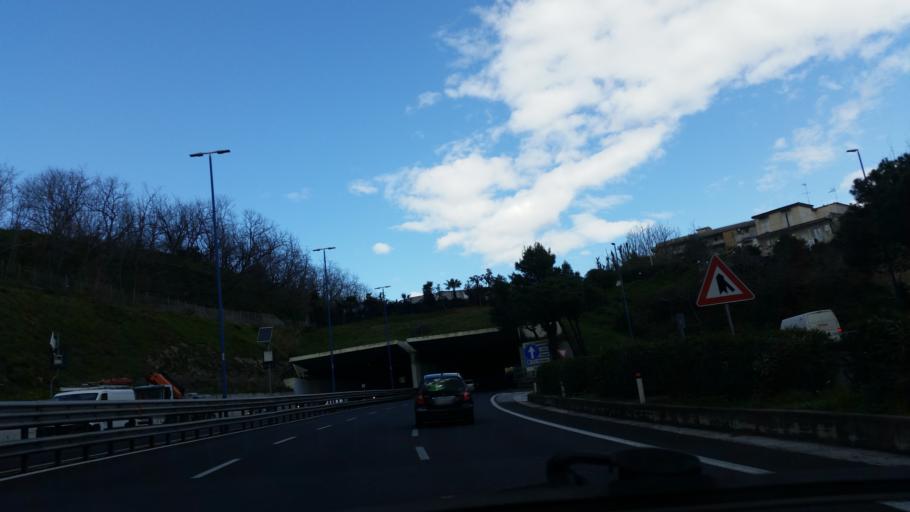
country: IT
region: Campania
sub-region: Provincia di Napoli
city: Napoli
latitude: 40.8513
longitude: 14.2151
